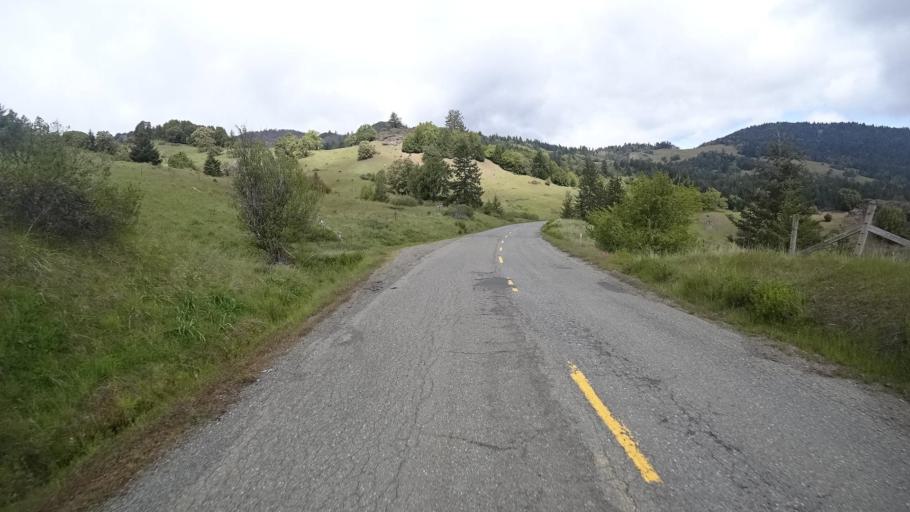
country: US
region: California
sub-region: Humboldt County
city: Redway
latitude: 40.1111
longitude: -123.6721
